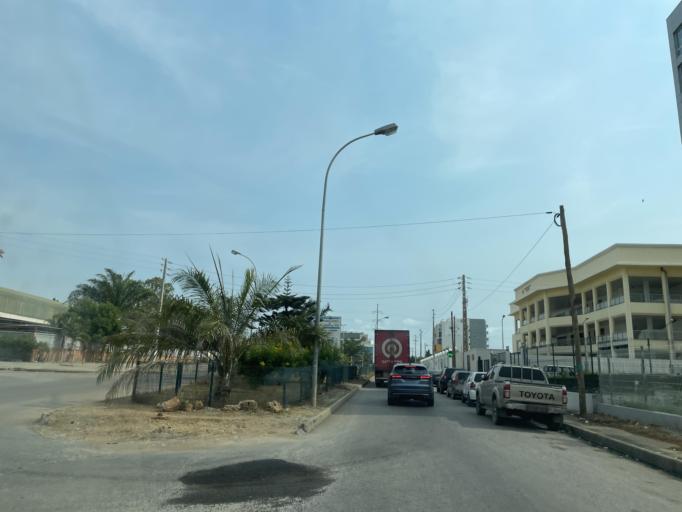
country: AO
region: Luanda
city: Luanda
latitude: -8.9041
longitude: 13.1974
